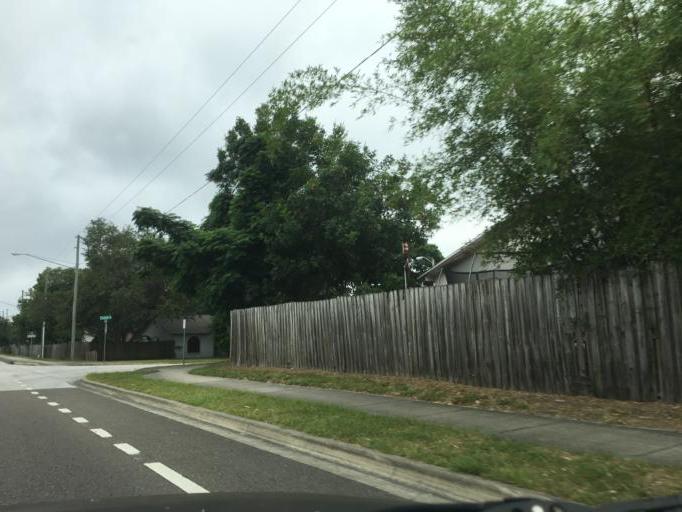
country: US
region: Florida
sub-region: Pinellas County
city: Dunedin
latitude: 28.0094
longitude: -82.7632
